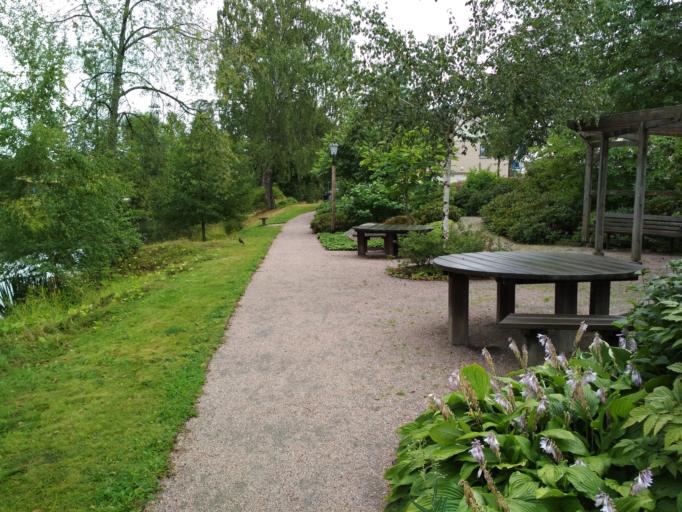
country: SE
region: Vaestmanland
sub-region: Kopings Kommun
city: Koping
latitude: 59.5162
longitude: 15.9898
